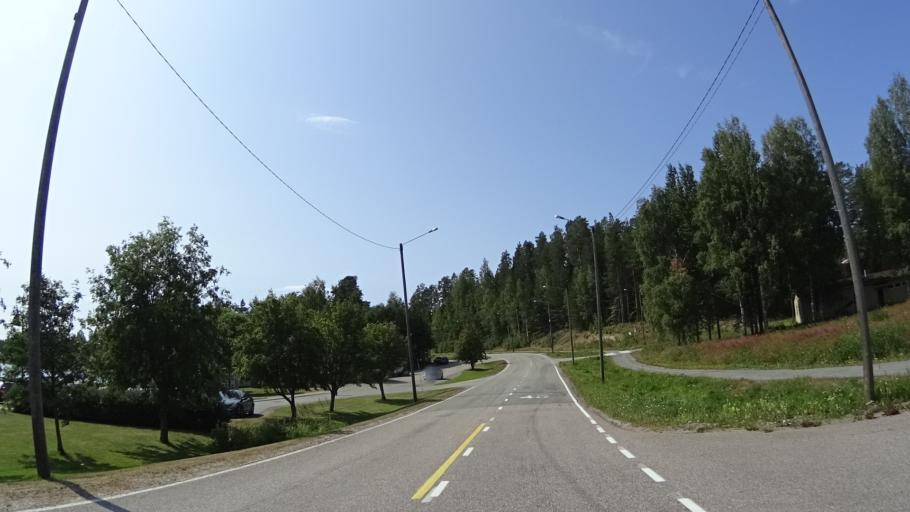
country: FI
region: Pirkanmaa
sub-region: Ylae-Pirkanmaa
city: Maenttae
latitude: 61.8599
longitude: 24.8273
